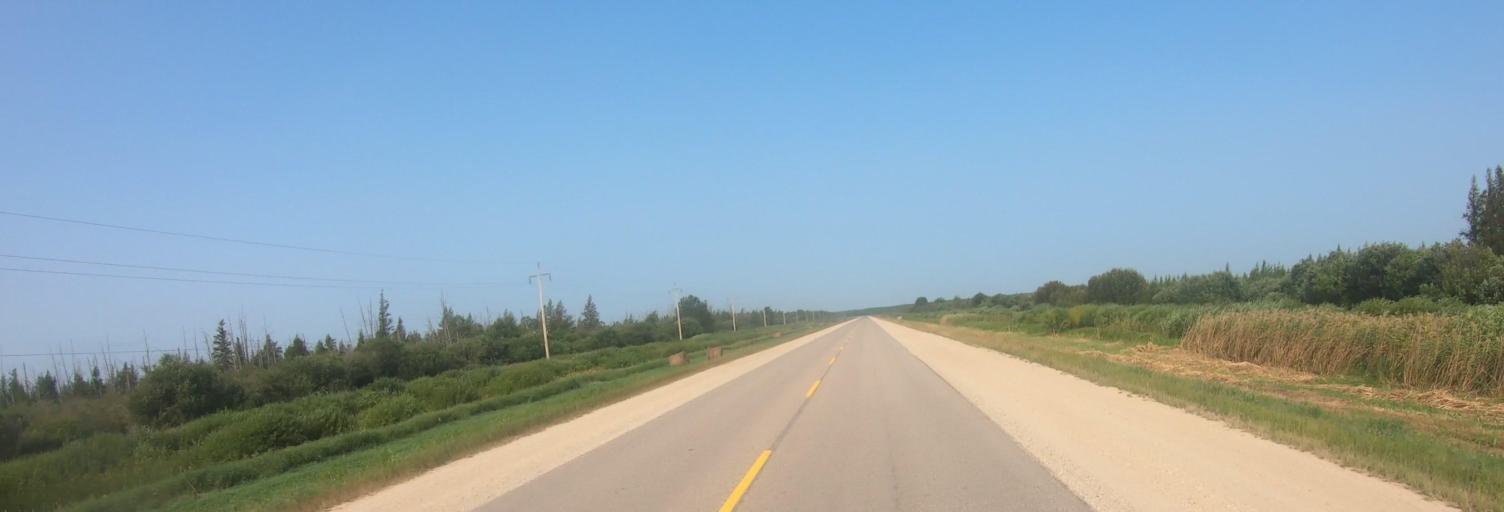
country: US
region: Minnesota
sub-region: Roseau County
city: Warroad
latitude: 49.0178
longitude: -95.5442
